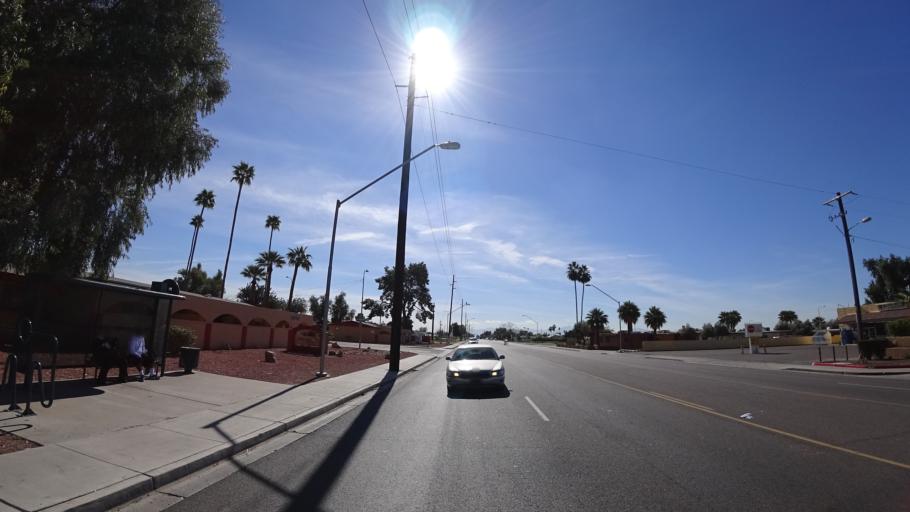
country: US
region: Arizona
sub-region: Maricopa County
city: Glendale
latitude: 33.5211
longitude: -112.2031
